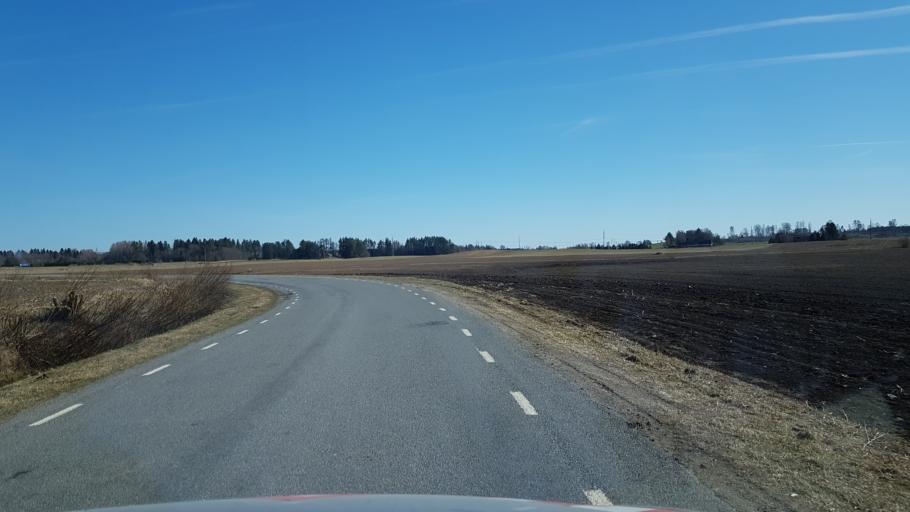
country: EE
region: Laeaene-Virumaa
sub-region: Someru vald
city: Someru
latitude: 59.3349
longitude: 26.5240
